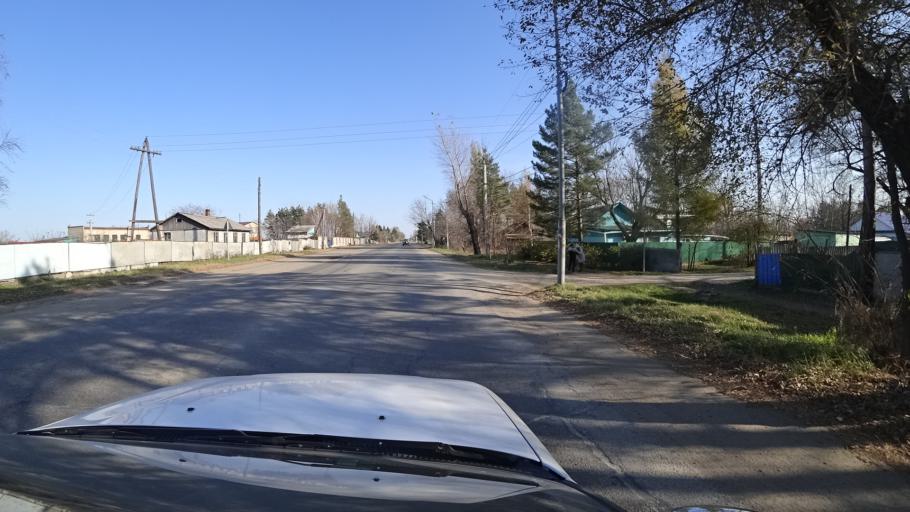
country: RU
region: Primorskiy
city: Dal'nerechensk
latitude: 45.9206
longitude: 133.7537
